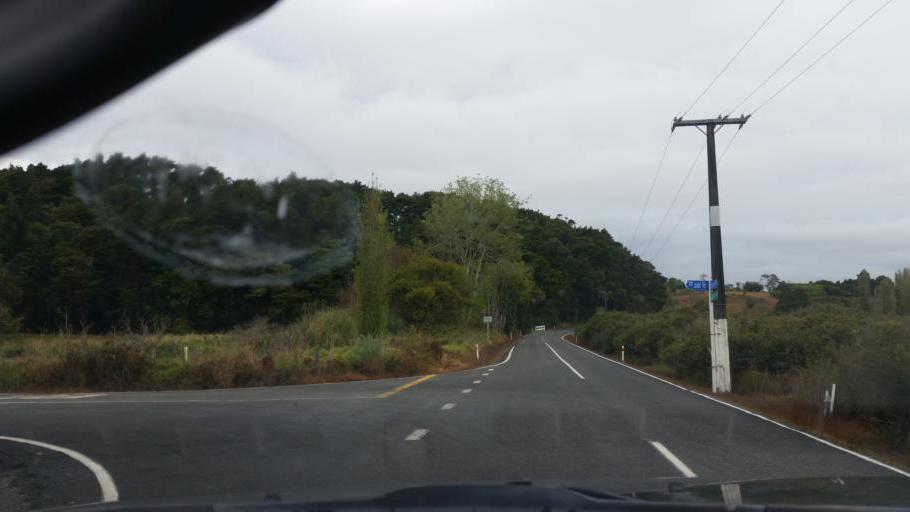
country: NZ
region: Auckland
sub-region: Auckland
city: Wellsford
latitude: -36.1221
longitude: 174.3618
